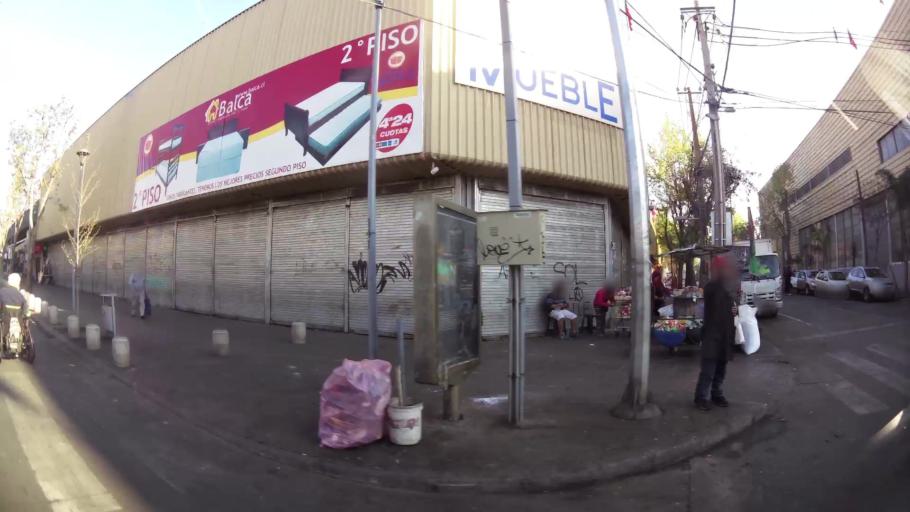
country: CL
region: Santiago Metropolitan
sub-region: Provincia de Santiago
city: Santiago
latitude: -33.4755
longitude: -70.6466
